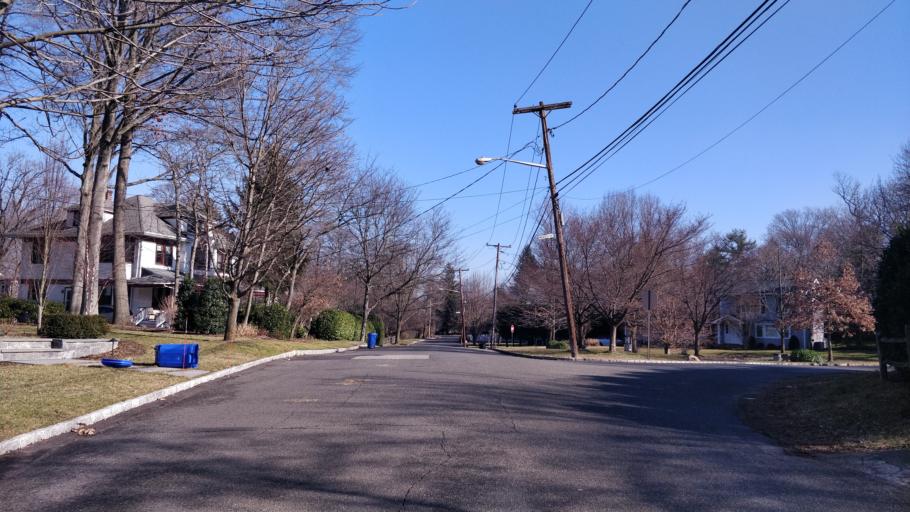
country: US
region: New York
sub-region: Nassau County
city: Sea Cliff
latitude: 40.8447
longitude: -73.6426
